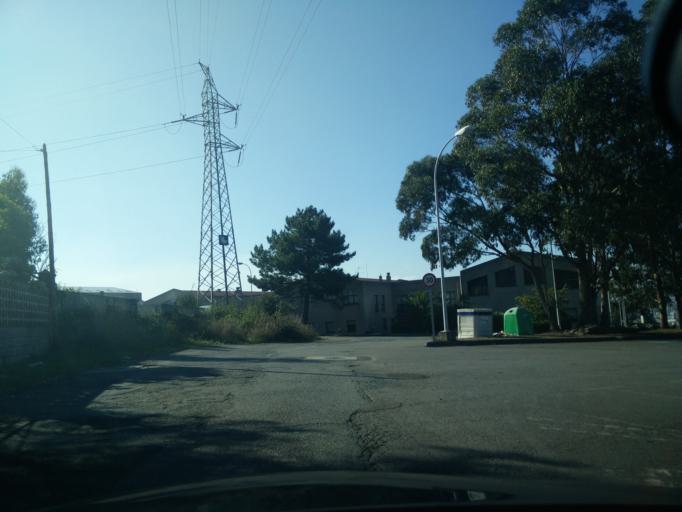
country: ES
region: Galicia
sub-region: Provincia da Coruna
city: Culleredo
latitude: 43.3252
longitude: -8.4063
